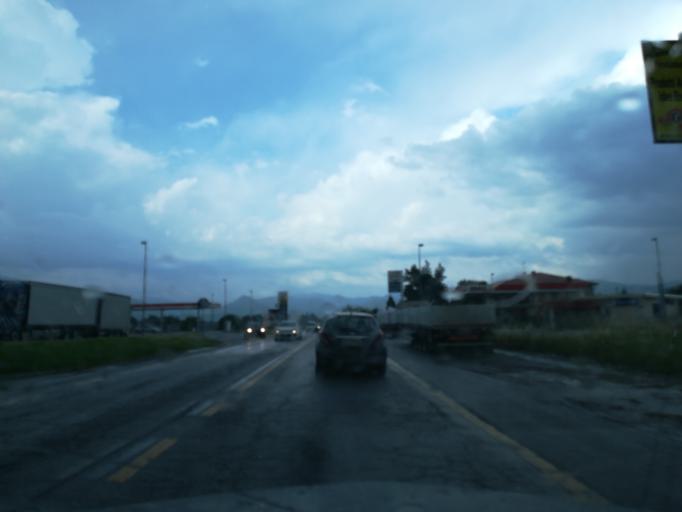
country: IT
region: Lombardy
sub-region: Provincia di Bergamo
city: Curno
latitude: 45.6851
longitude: 9.6023
